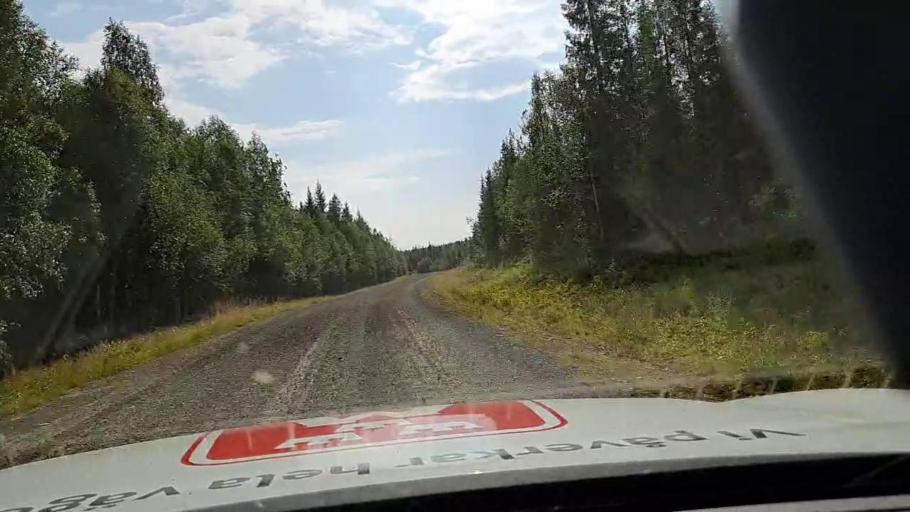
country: SE
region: Vaesterbotten
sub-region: Storumans Kommun
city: Fristad
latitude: 65.5427
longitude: 16.7972
